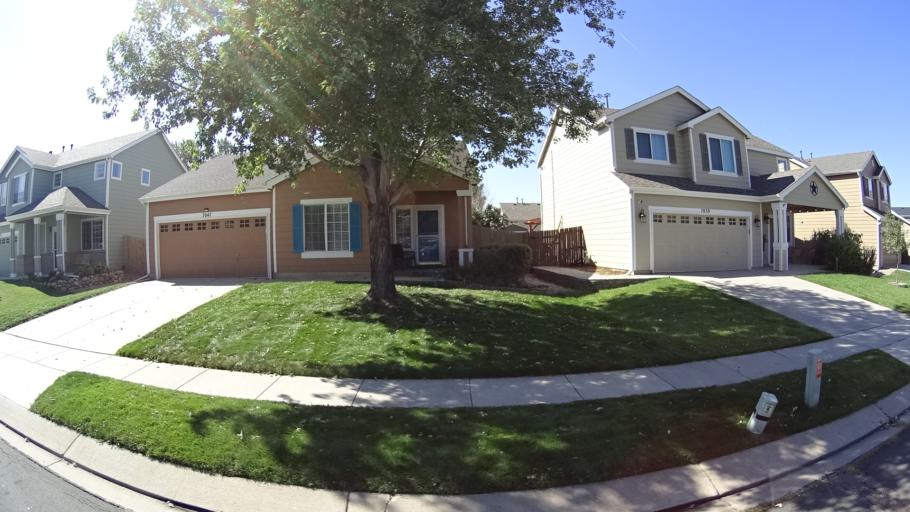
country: US
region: Colorado
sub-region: El Paso County
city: Cimarron Hills
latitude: 38.8823
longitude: -104.6955
